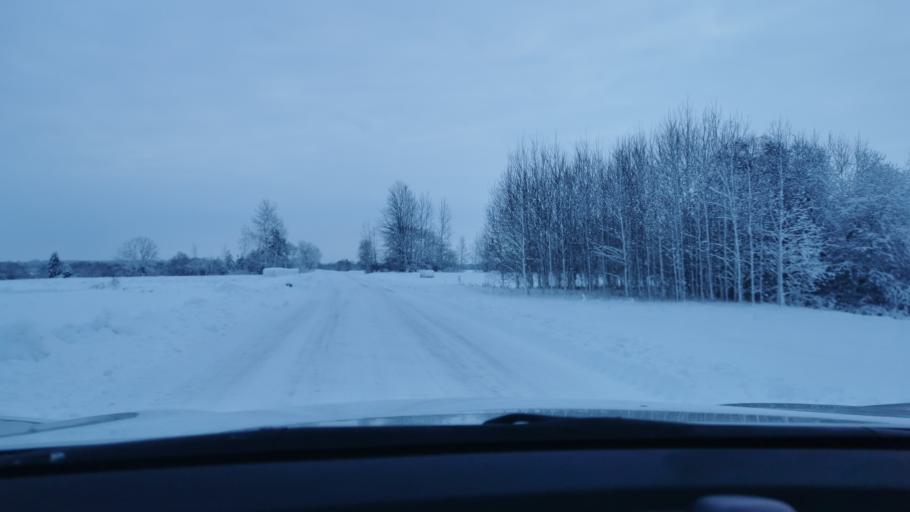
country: EE
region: Laeaene-Virumaa
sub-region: Haljala vald
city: Haljala
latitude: 59.4914
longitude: 26.3175
